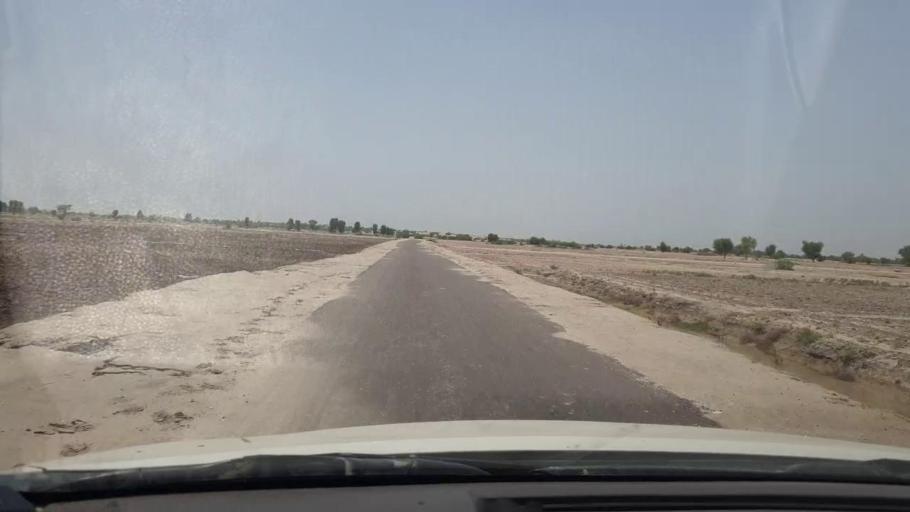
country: PK
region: Sindh
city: Rohri
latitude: 27.5206
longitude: 69.1592
